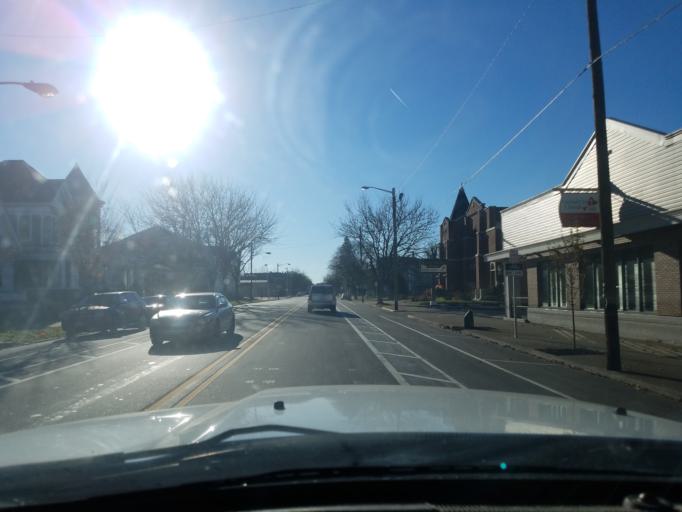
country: US
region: Indiana
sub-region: Floyd County
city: New Albany
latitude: 38.2913
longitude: -85.8098
